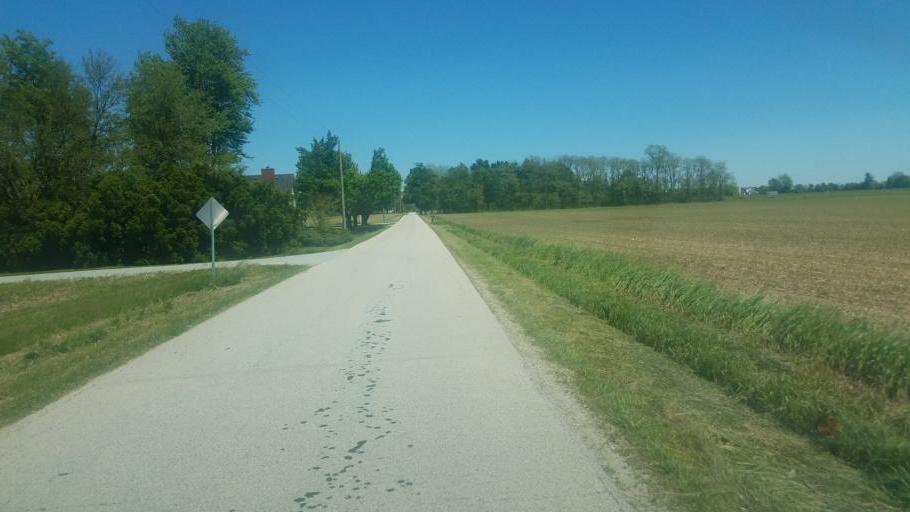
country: US
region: Ohio
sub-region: Champaign County
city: Saint Paris
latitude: 40.1993
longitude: -84.0399
